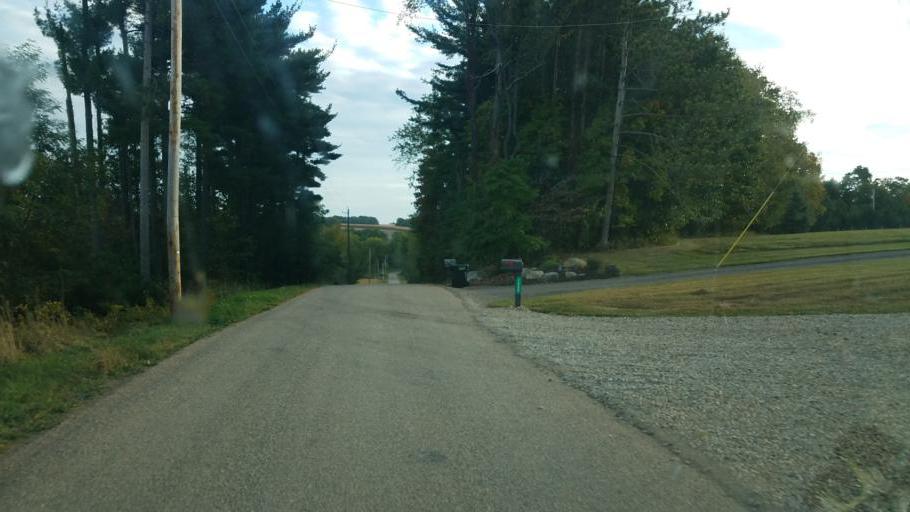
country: US
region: Ohio
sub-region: Ashland County
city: Loudonville
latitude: 40.7027
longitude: -82.1855
